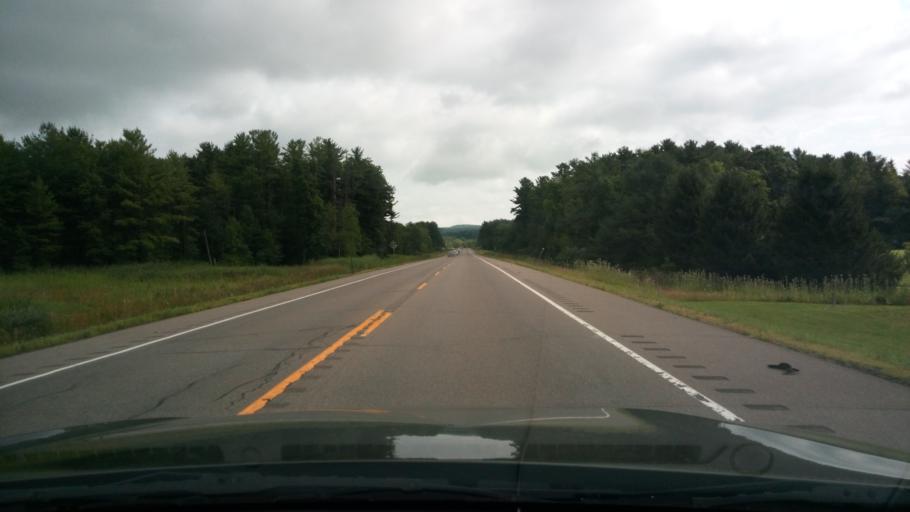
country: US
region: New York
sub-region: Chemung County
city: Horseheads North
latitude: 42.2054
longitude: -76.7770
